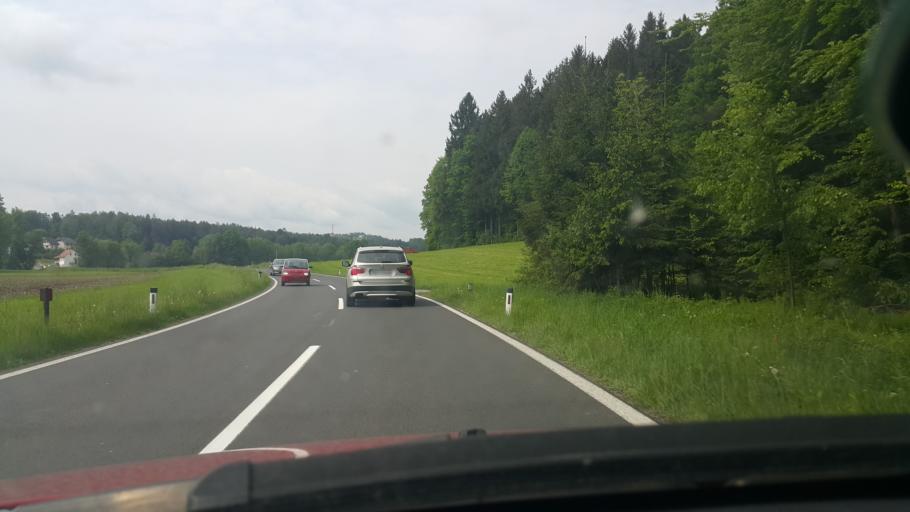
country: AT
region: Styria
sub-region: Politischer Bezirk Graz-Umgebung
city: Hitzendorf
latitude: 47.0502
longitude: 15.2929
